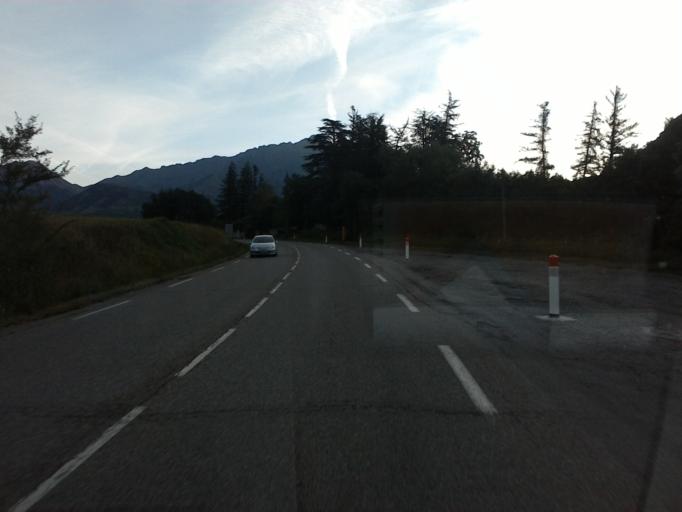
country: FR
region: Provence-Alpes-Cote d'Azur
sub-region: Departement des Hautes-Alpes
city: Saint-Bonnet-en-Champsaur
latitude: 44.7437
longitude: 6.0071
